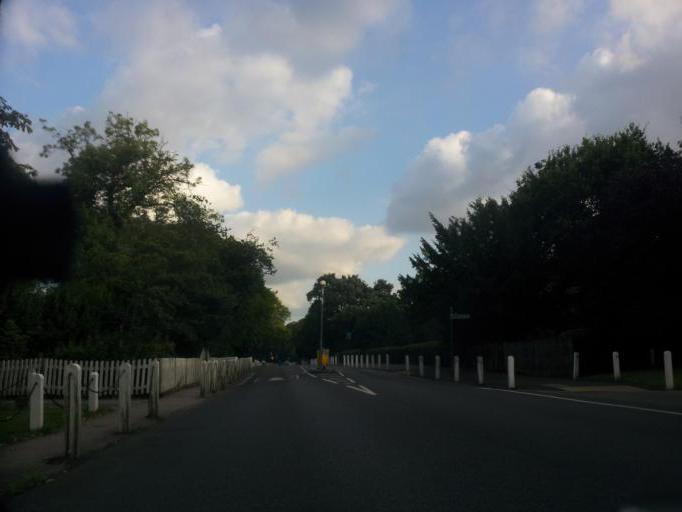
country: GB
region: England
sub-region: Greater London
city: Brixton
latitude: 51.4443
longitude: -0.0851
